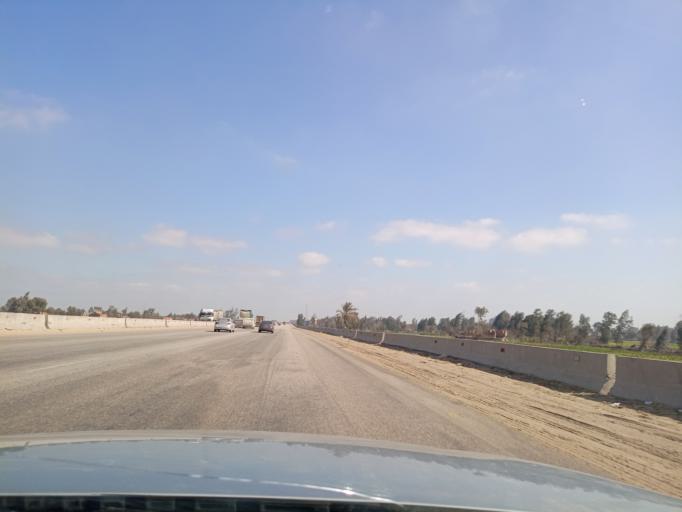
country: EG
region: Muhafazat al Minufiyah
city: Al Bajur
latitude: 30.4322
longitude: 31.1010
